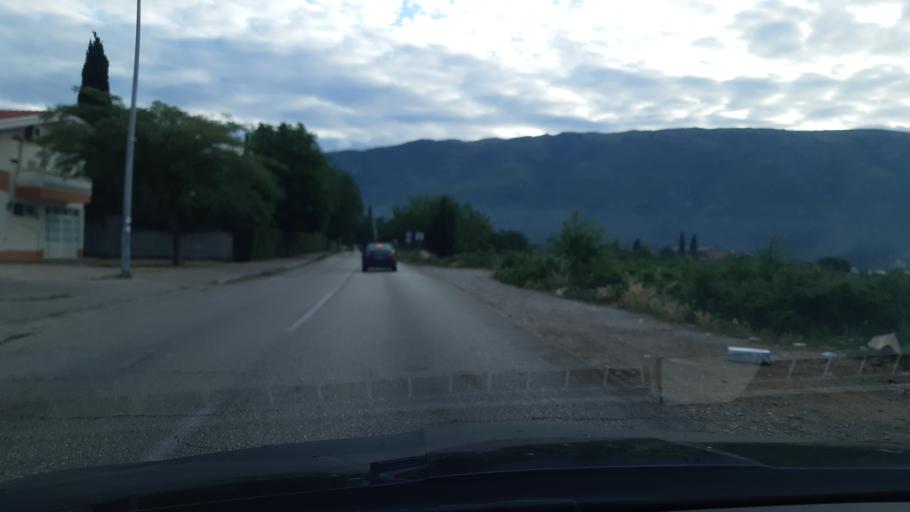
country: BA
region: Federation of Bosnia and Herzegovina
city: Rodoc
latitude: 43.3148
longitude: 17.8162
